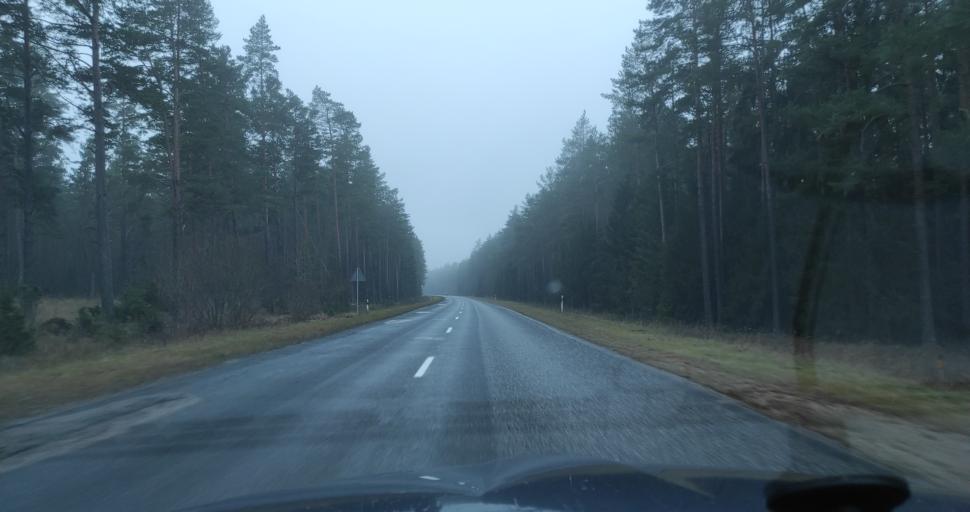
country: LV
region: Alsunga
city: Alsunga
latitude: 57.0227
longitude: 21.4003
